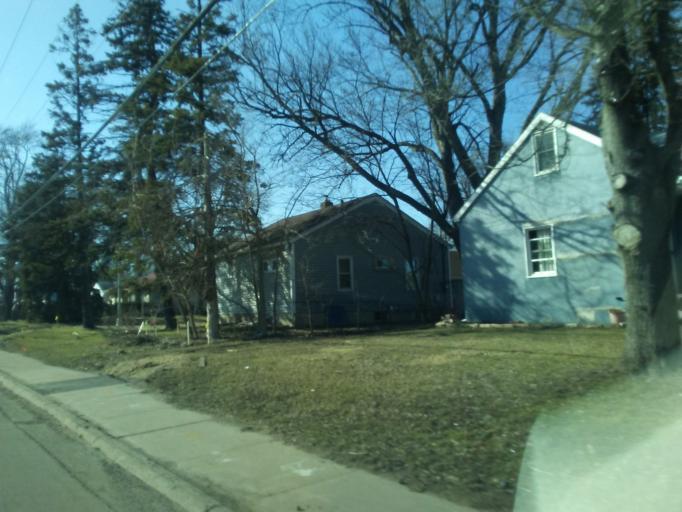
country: US
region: Minnesota
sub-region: Hennepin County
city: Richfield
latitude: 44.8835
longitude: -93.2991
